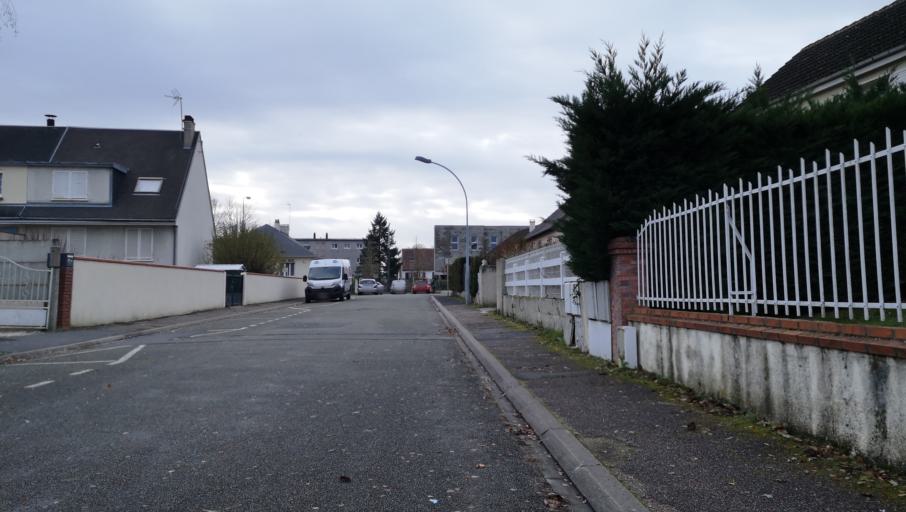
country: FR
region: Centre
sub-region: Departement du Loiret
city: Saint-Jean-de-Braye
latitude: 47.9103
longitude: 1.9617
